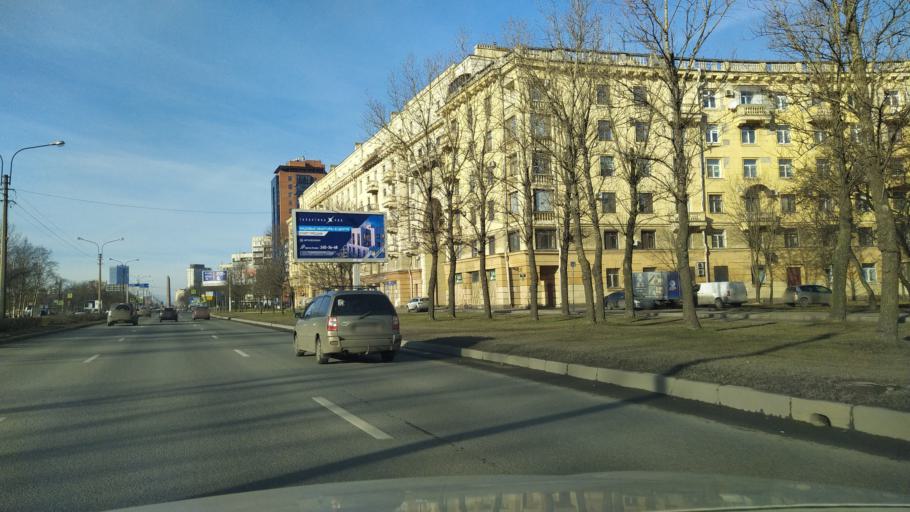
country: RU
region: St.-Petersburg
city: Kupchino
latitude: 59.8358
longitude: 30.3352
